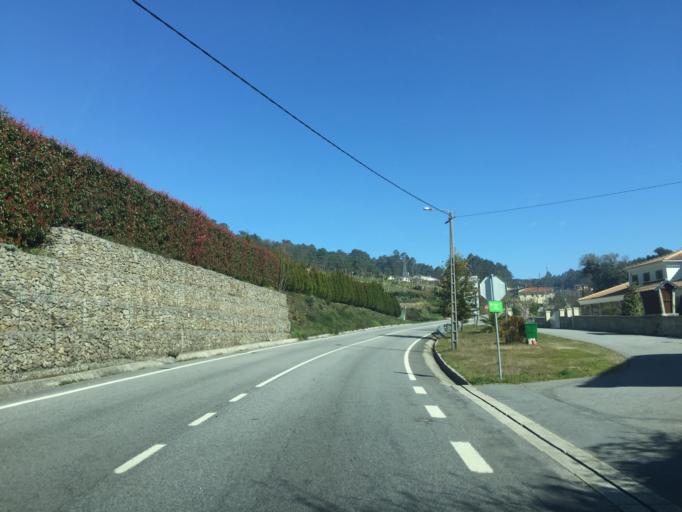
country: PT
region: Aveiro
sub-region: Vale de Cambra
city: Macieira de Cambra
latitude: 40.8846
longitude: -8.3636
